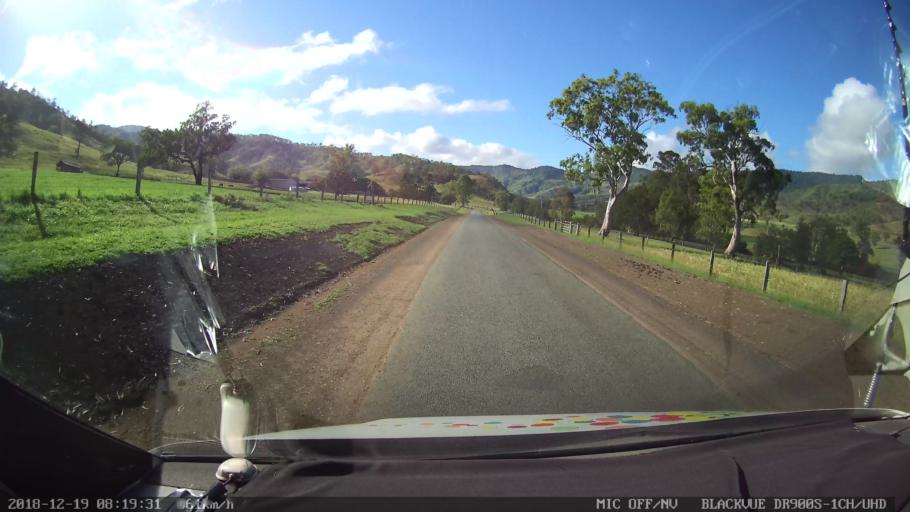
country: AU
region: New South Wales
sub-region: Kyogle
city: Kyogle
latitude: -28.2826
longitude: 152.9093
